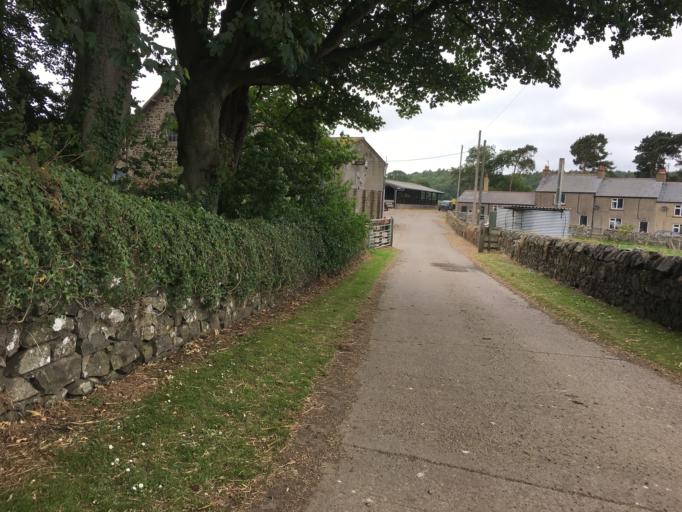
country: GB
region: England
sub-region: Northumberland
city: Belford
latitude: 55.6083
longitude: -1.8669
